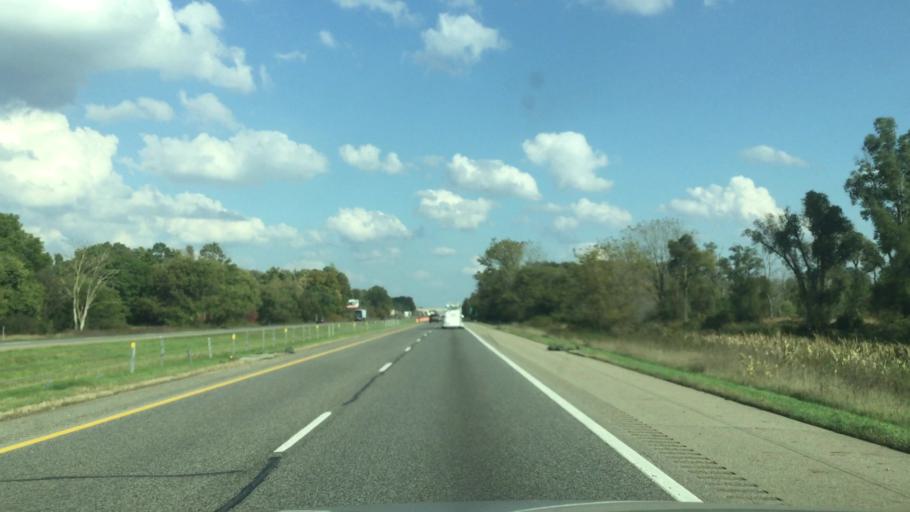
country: US
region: Michigan
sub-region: Calhoun County
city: Marshall
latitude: 42.2976
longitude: -85.0514
